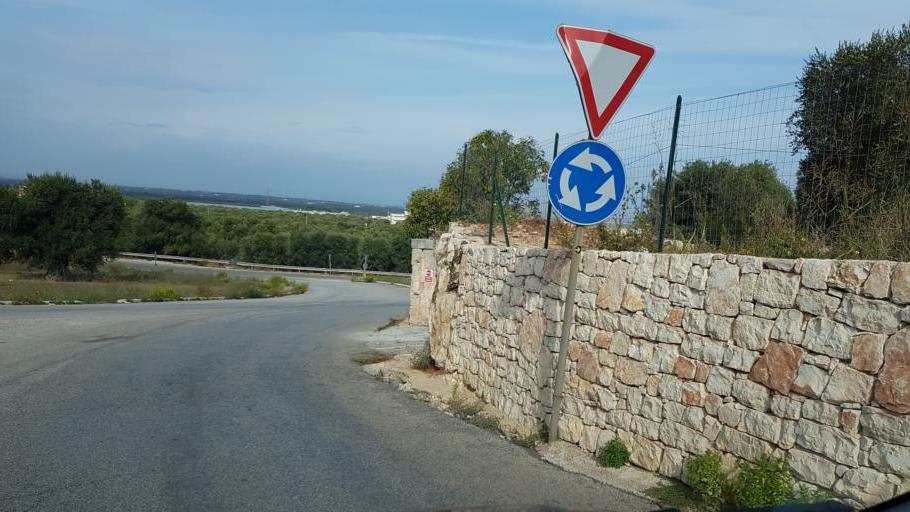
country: IT
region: Apulia
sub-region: Provincia di Brindisi
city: Ostuni
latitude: 40.7396
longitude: 17.5776
